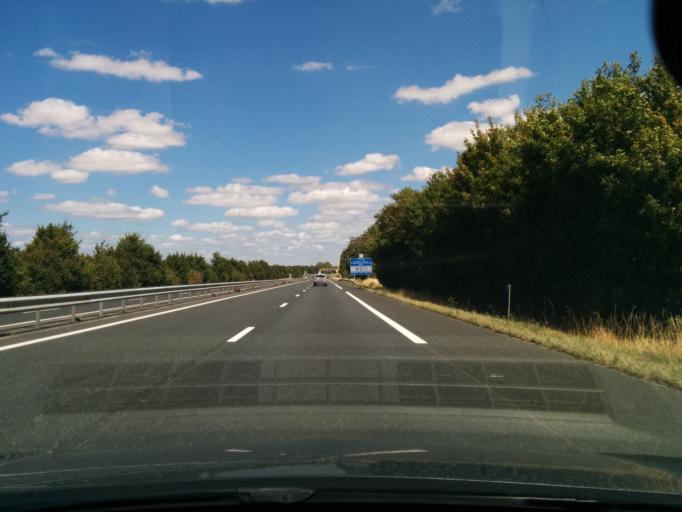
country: FR
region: Centre
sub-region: Departement de l'Indre
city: Vatan
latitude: 47.0854
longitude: 1.8356
